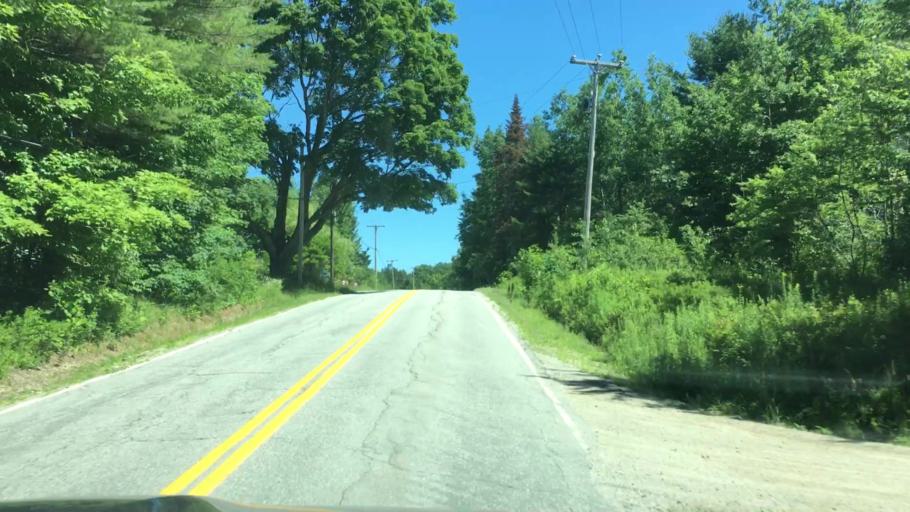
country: US
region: Maine
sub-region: Hancock County
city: Penobscot
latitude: 44.5149
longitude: -68.6711
